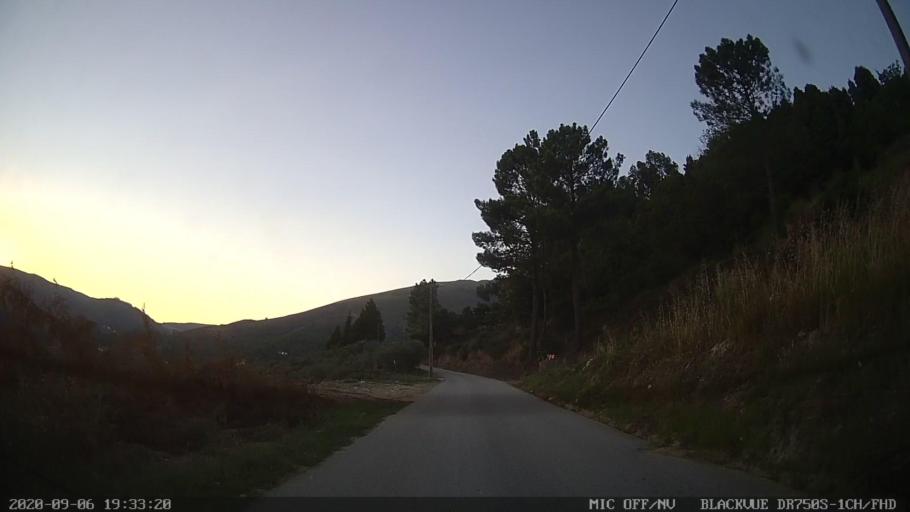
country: PT
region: Vila Real
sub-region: Mesao Frio
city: Mesao Frio
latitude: 41.1759
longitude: -7.9001
